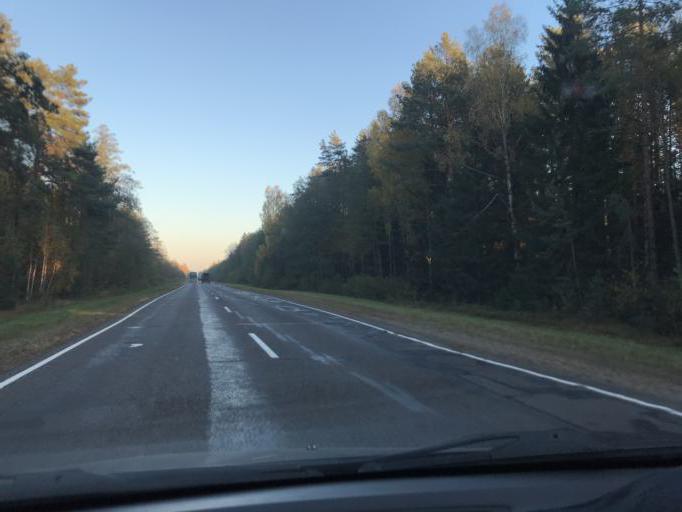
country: BY
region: Minsk
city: Staryya Darohi
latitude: 53.0437
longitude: 28.1359
